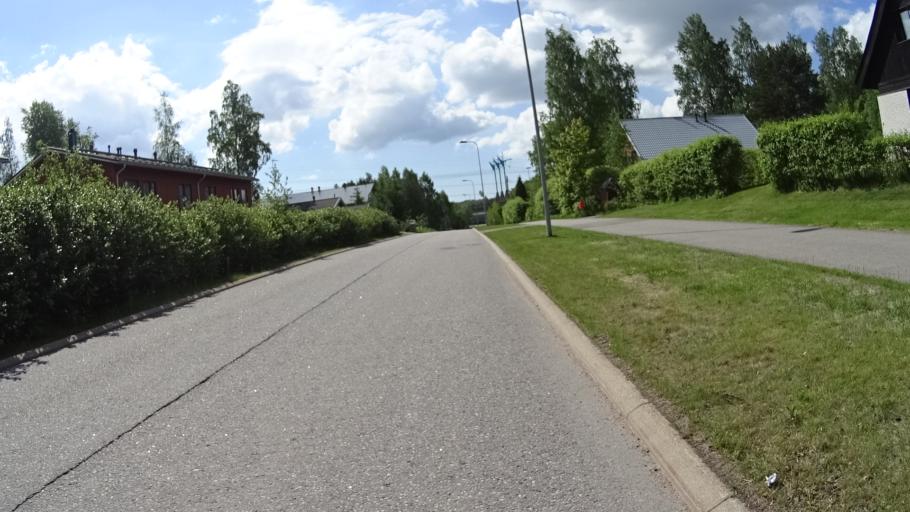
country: FI
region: Uusimaa
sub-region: Helsinki
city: Espoo
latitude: 60.2228
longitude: 24.6417
